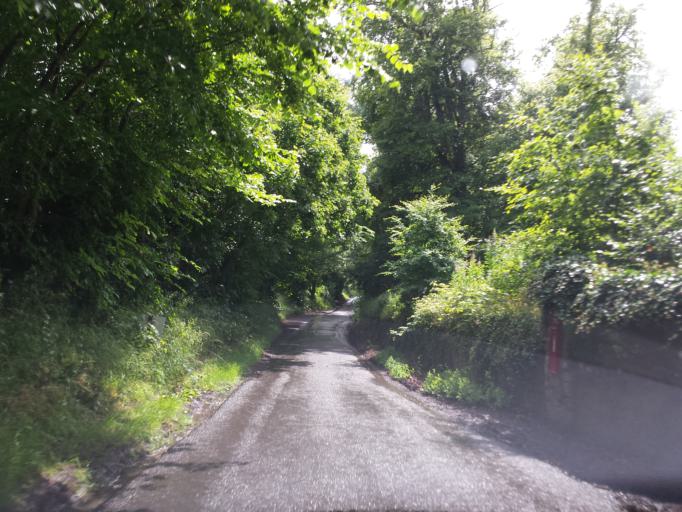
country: GB
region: Scotland
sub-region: The Scottish Borders
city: Saint Boswells
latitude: 55.5931
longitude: -2.6447
